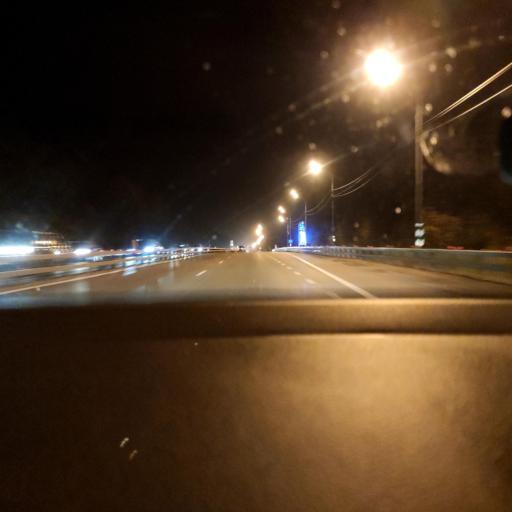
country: RU
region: Moskovskaya
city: Selyatino
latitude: 55.5059
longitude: 36.9797
